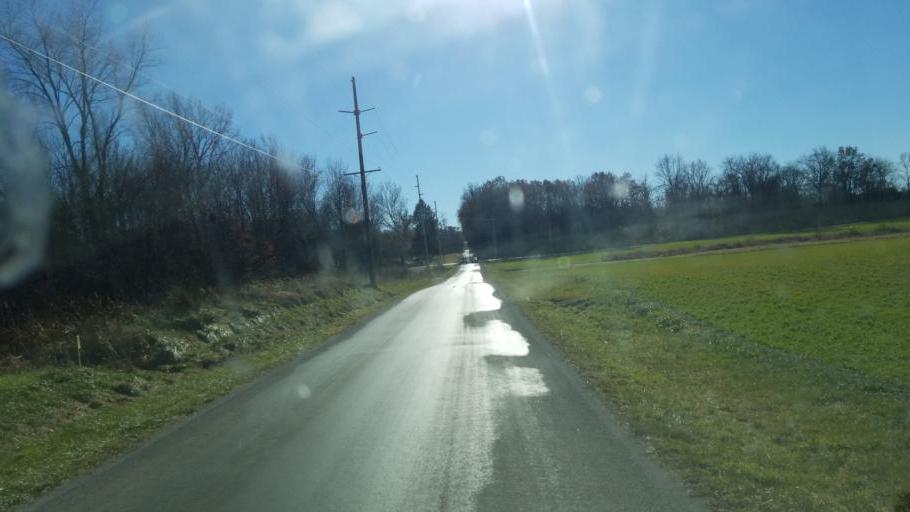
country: US
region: Ohio
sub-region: Huron County
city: Plymouth
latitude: 40.9613
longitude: -82.6958
